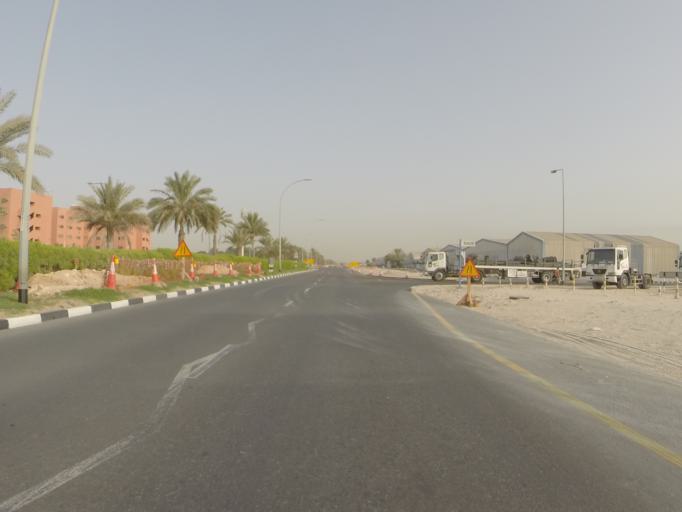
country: AE
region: Dubai
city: Dubai
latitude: 24.9591
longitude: 55.0596
